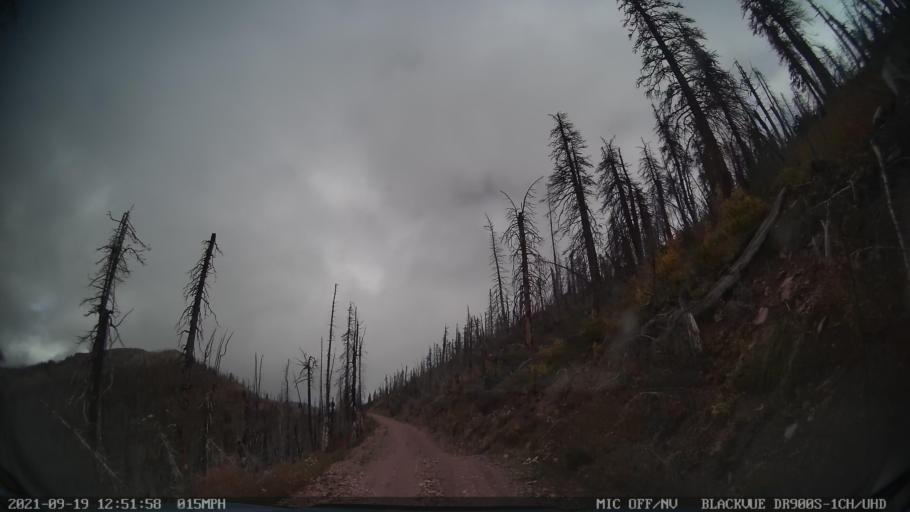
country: US
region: Montana
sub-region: Missoula County
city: Seeley Lake
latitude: 47.1913
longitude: -113.3583
